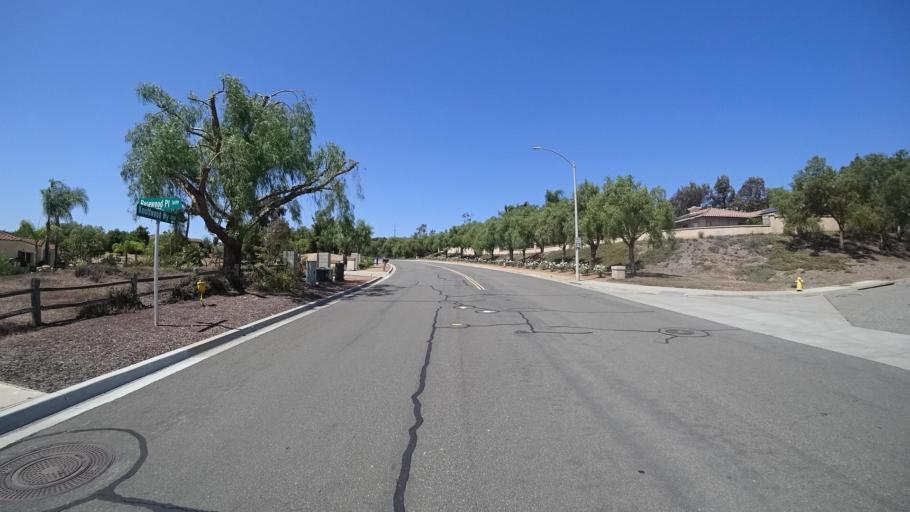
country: US
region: California
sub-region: San Diego County
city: Bonsall
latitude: 33.3275
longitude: -117.1942
